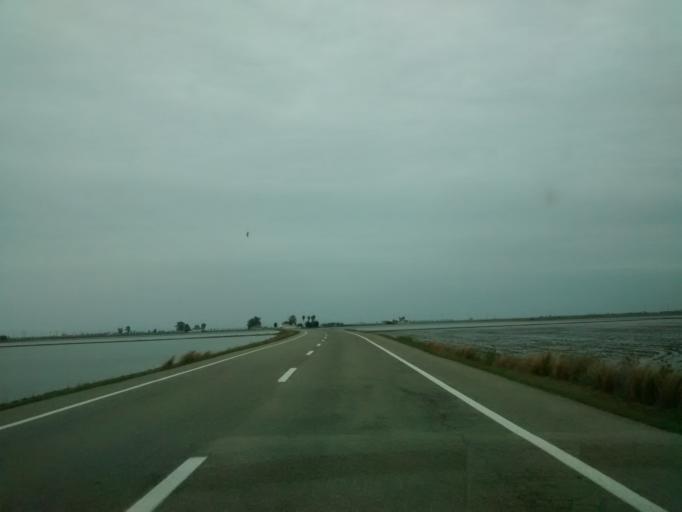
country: ES
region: Catalonia
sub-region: Provincia de Tarragona
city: Deltebre
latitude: 40.6890
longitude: 0.6858
